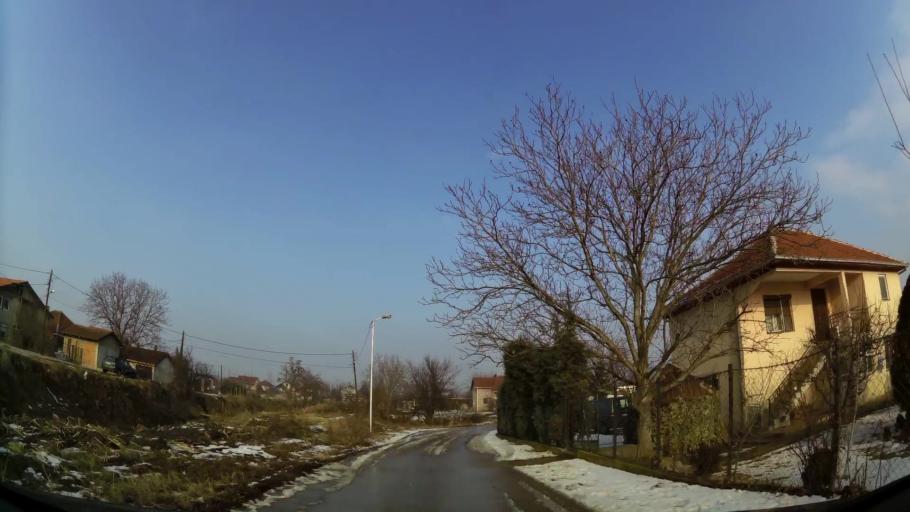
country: MK
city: Miladinovci
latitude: 41.9747
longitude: 21.6446
